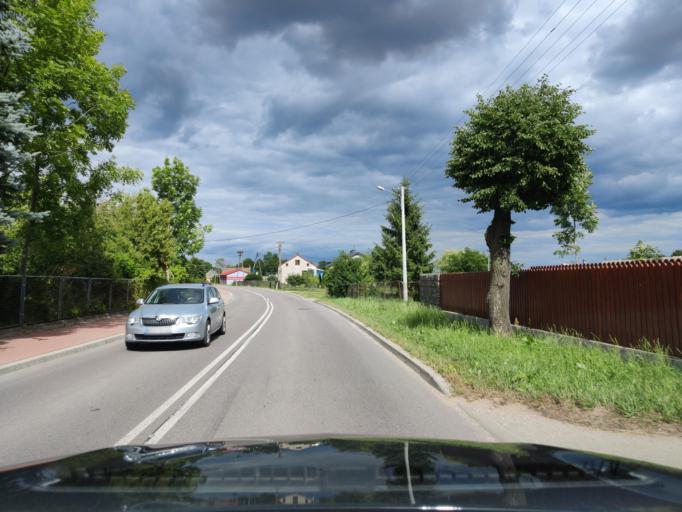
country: PL
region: Masovian Voivodeship
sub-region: Powiat sokolowski
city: Ceranow
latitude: 52.6107
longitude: 22.1980
